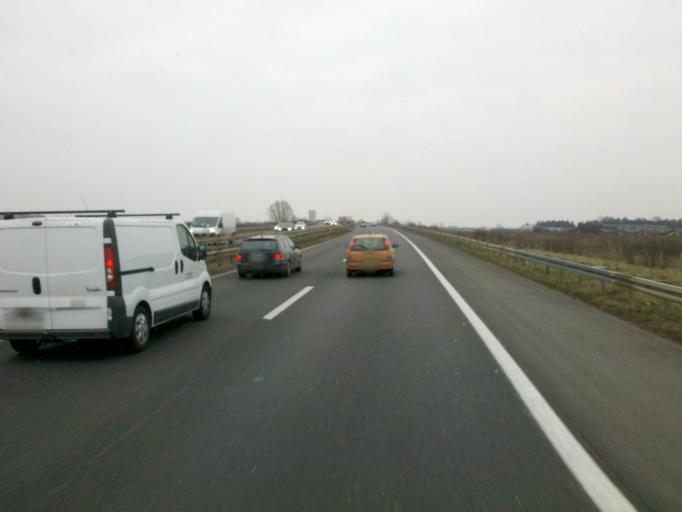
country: HR
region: Grad Zagreb
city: Zadvorsko
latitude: 45.7510
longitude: 15.9112
